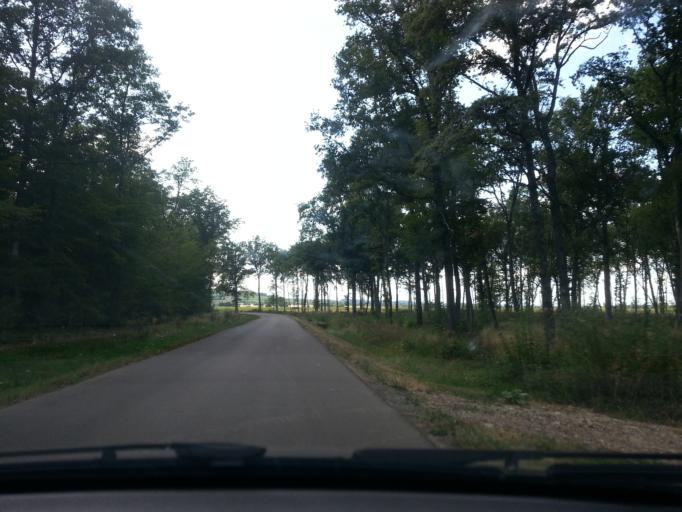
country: FR
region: Bourgogne
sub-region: Departement de Saone-et-Loire
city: Dracy-le-Fort
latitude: 46.7720
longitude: 4.7667
